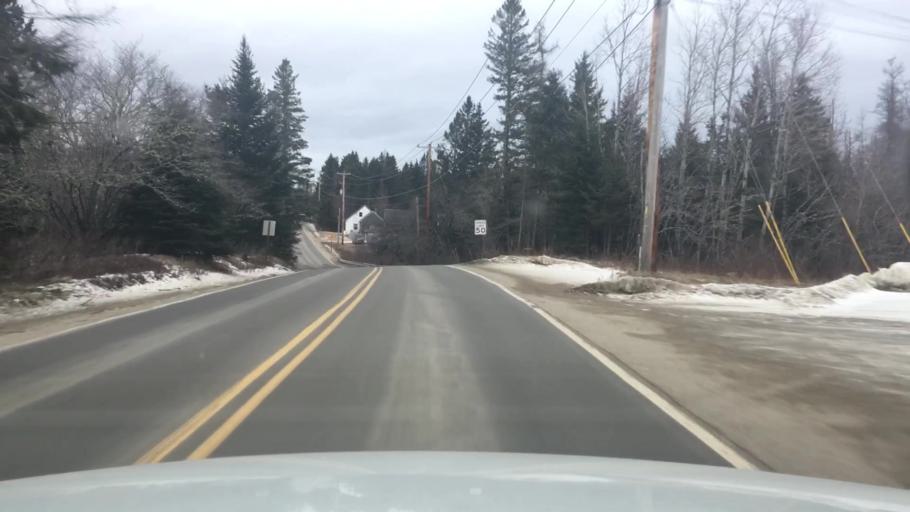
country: US
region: Maine
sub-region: Washington County
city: Addison
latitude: 44.6245
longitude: -67.7116
